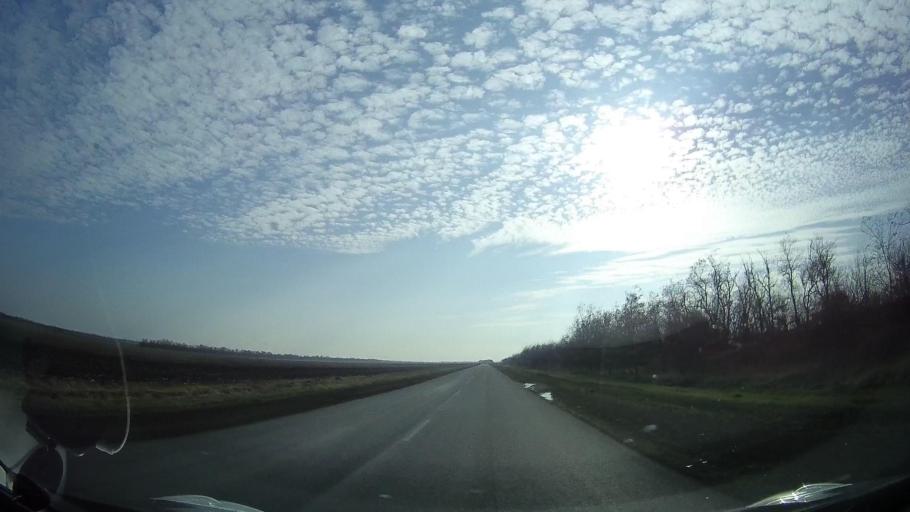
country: RU
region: Rostov
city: Veselyy
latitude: 46.9747
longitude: 40.7198
